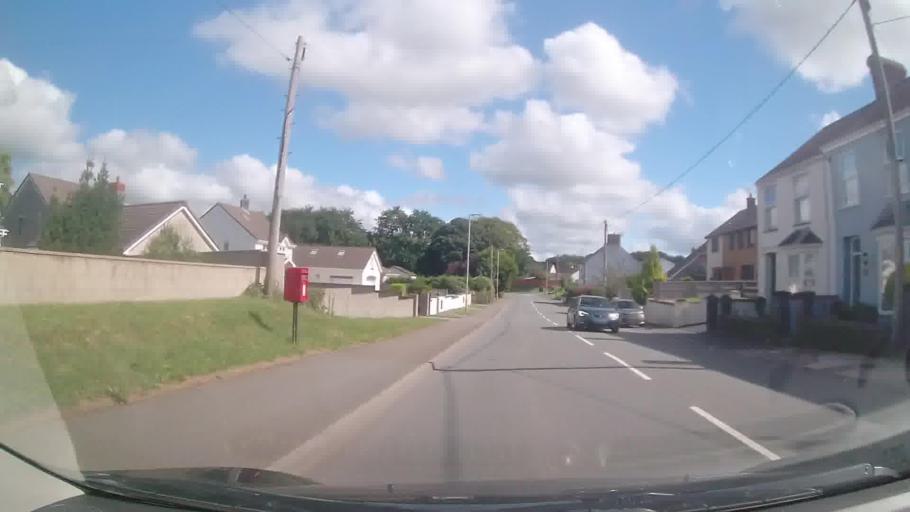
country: GB
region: Wales
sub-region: Pembrokeshire
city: Pembroke
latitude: 51.6760
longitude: -4.9038
